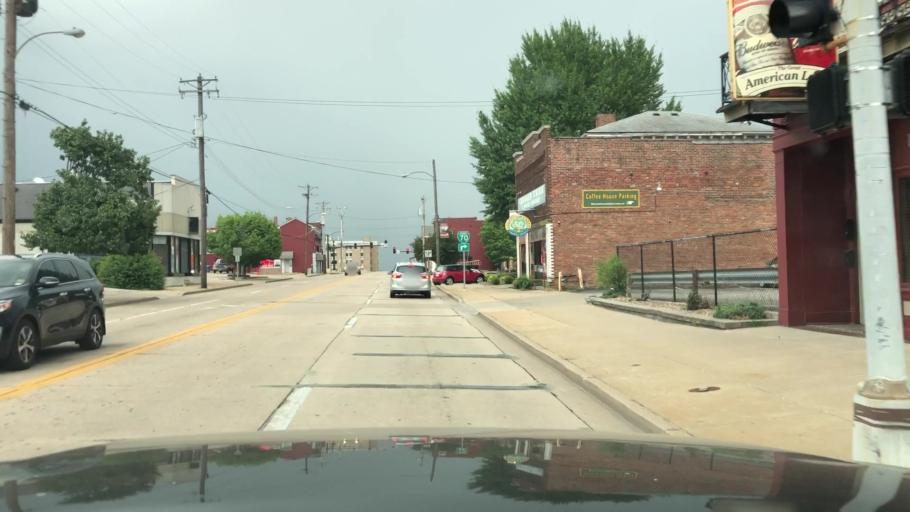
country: US
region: Missouri
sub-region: Saint Charles County
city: Saint Charles
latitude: 38.7818
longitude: -90.4892
